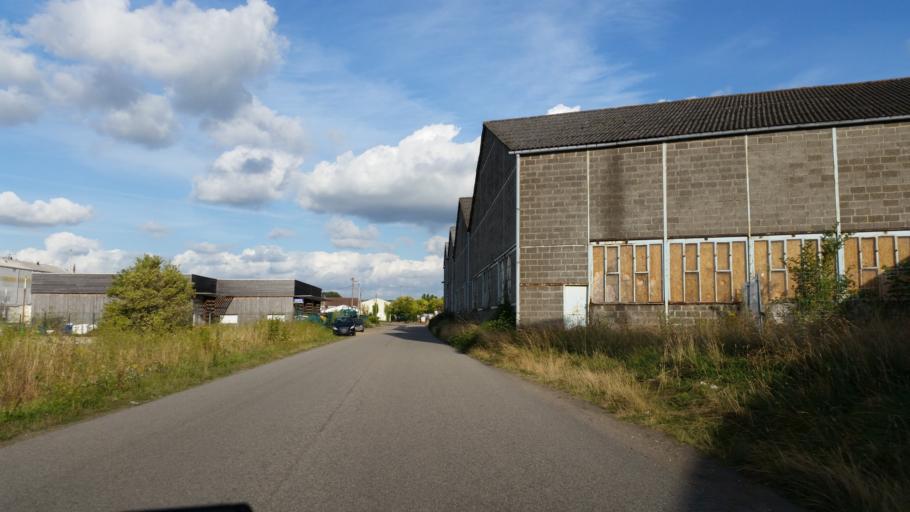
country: FR
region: Lower Normandy
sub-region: Departement du Calvados
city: Honfleur
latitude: 49.4158
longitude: 0.2482
